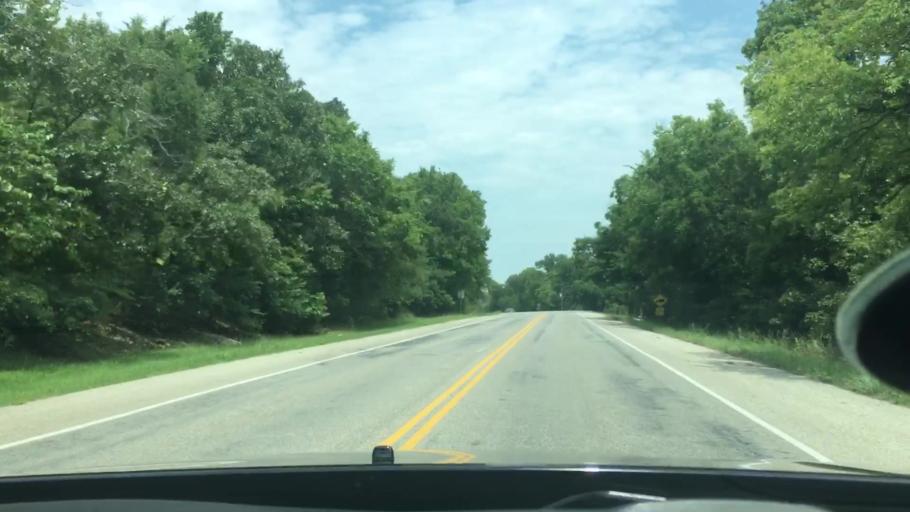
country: US
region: Oklahoma
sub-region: Pontotoc County
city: Byng
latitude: 34.8359
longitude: -96.6789
